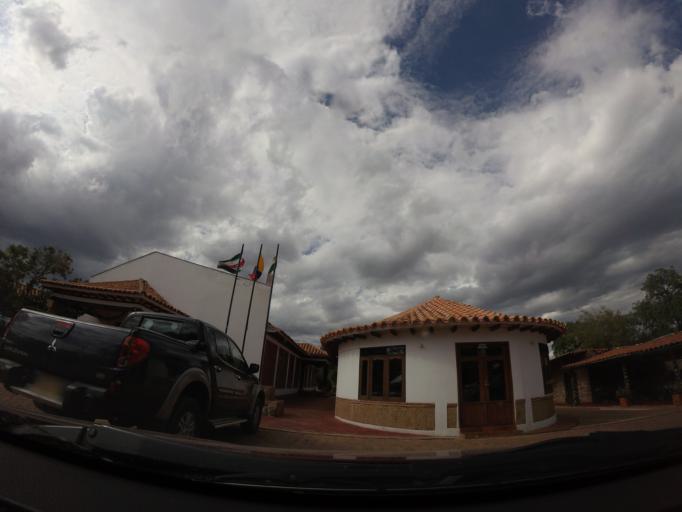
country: CO
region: Boyaca
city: Sachica
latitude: 5.5863
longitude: -73.5385
